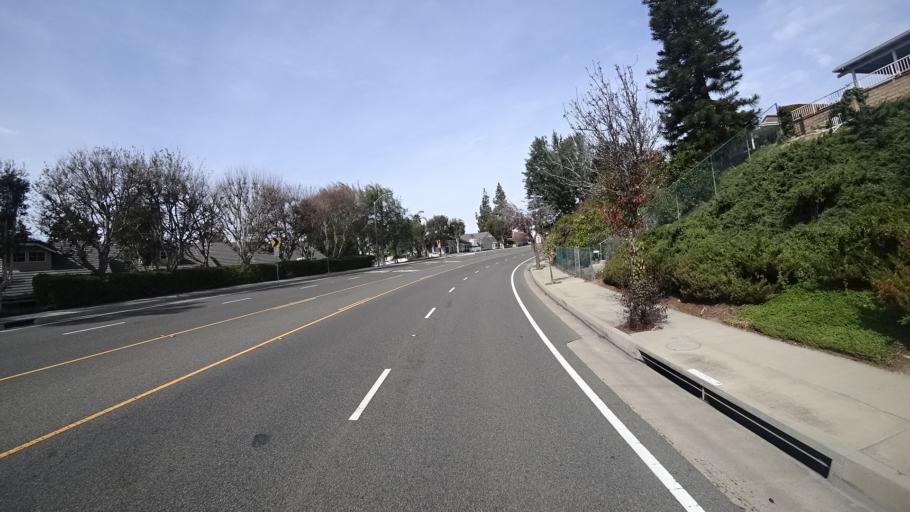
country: US
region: California
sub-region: Orange County
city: Villa Park
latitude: 33.8310
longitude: -117.8335
